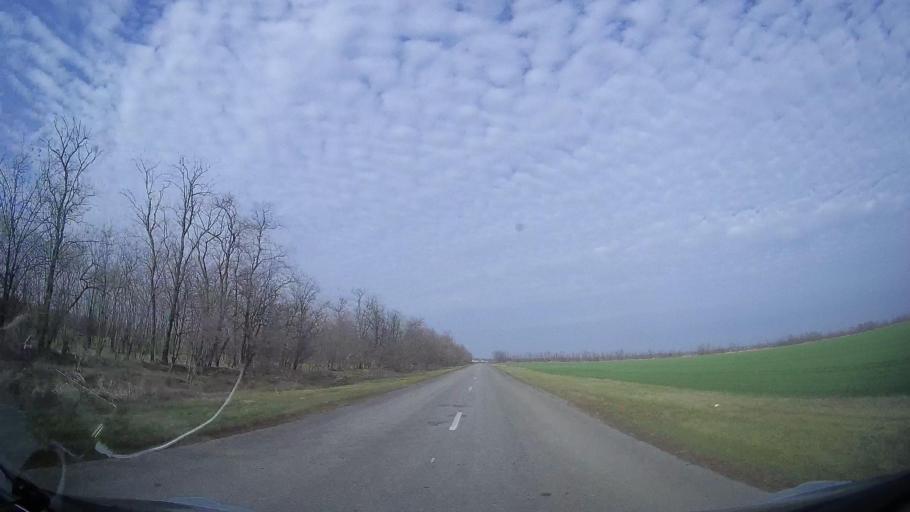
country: RU
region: Rostov
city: Gigant
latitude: 46.8736
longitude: 41.2733
